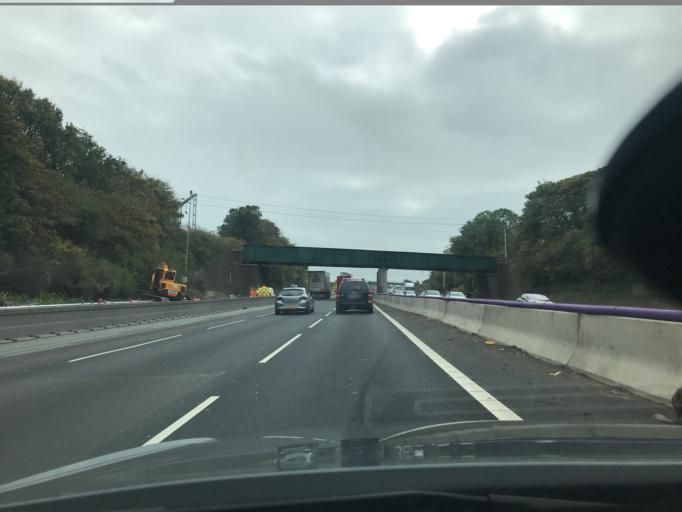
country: GB
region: England
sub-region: Cheshire East
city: Holmes Chapel
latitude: 53.1826
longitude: -2.3696
